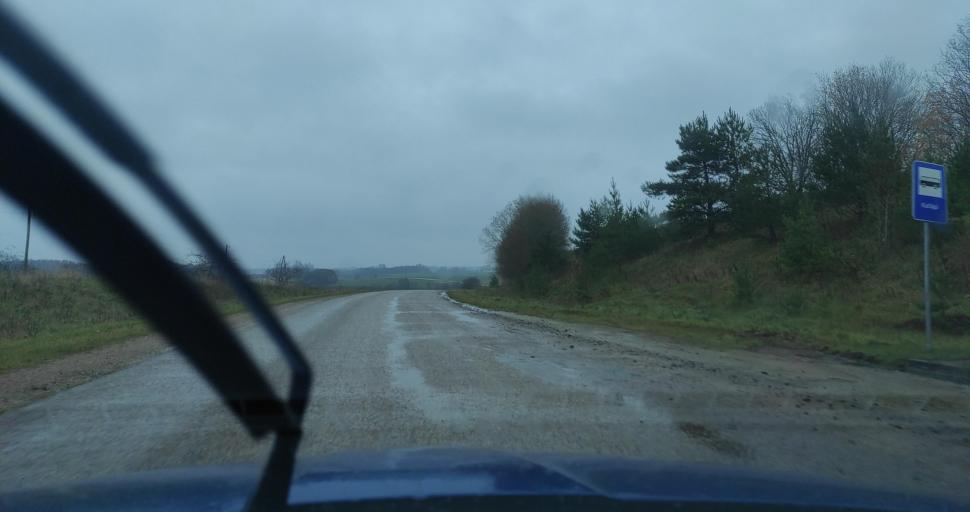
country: LV
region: Alsunga
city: Alsunga
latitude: 56.8966
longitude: 21.6096
